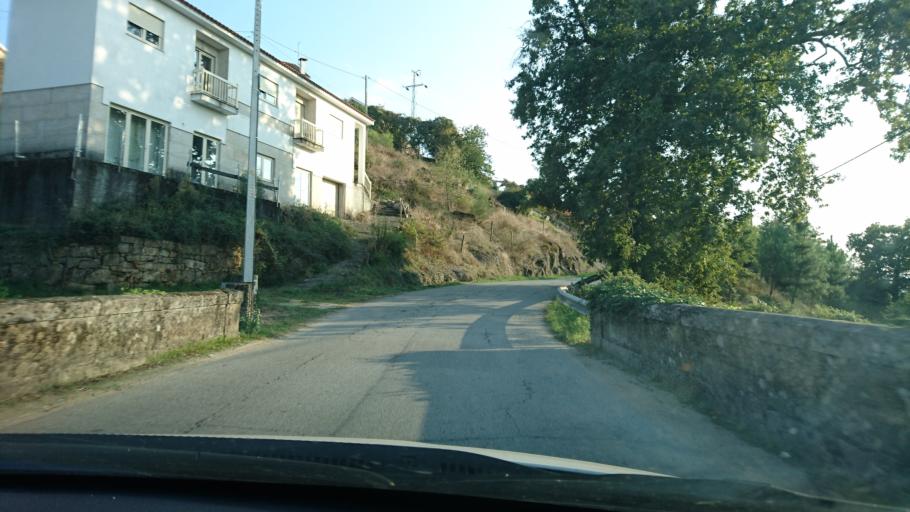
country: PT
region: Vila Real
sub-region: Mondim de Basto
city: Mondim de Basto
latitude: 41.4419
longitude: -7.9263
